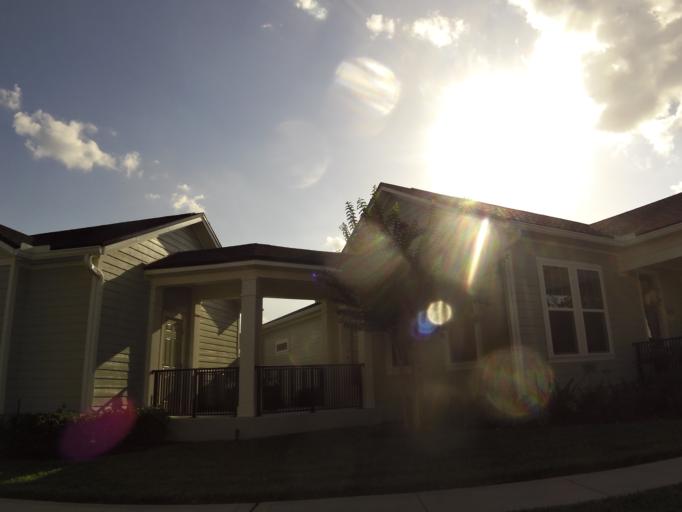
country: US
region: Florida
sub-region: Clay County
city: Green Cove Springs
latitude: 30.0229
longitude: -81.6334
